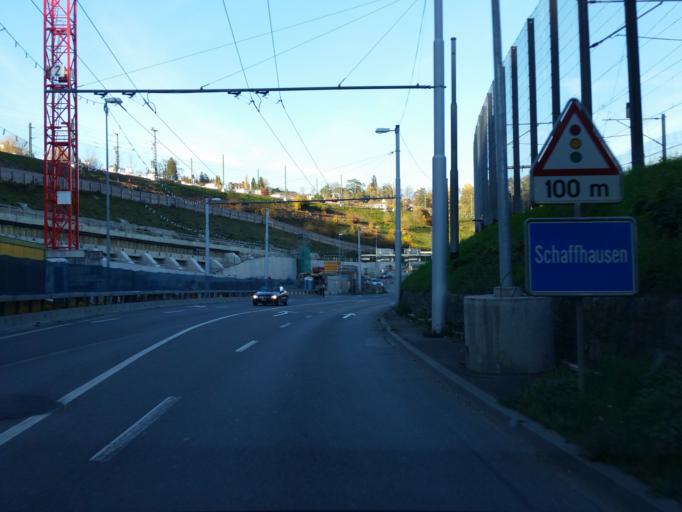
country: CH
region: Schaffhausen
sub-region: Bezirk Schaffhausen
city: Neuhausen
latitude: 47.6915
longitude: 8.6220
